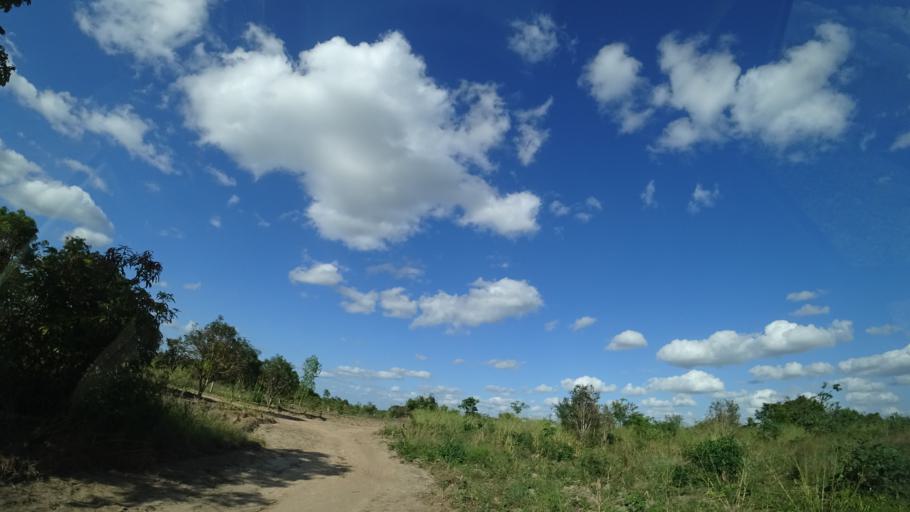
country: MZ
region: Sofala
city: Dondo
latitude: -19.4245
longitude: 34.7206
